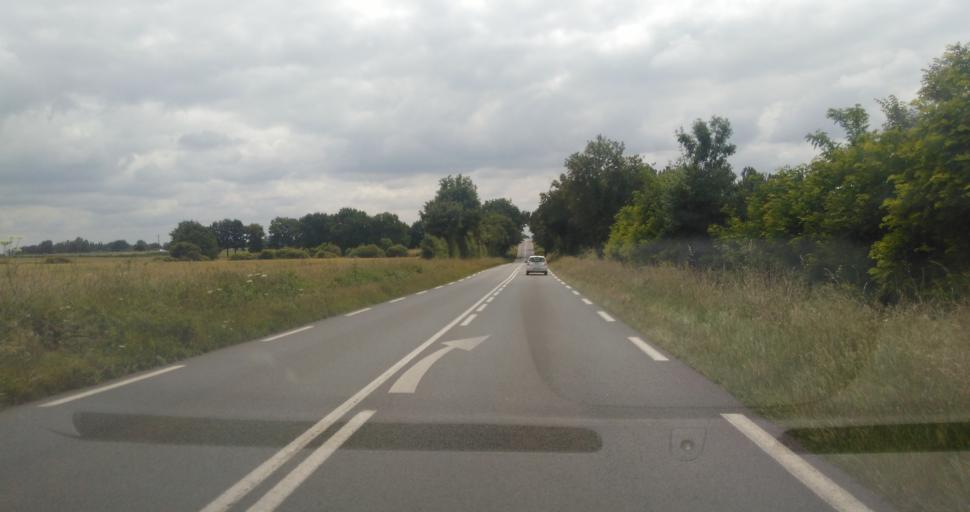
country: FR
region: Pays de la Loire
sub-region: Departement de la Vendee
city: Bournezeau
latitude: 46.6116
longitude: -1.1453
